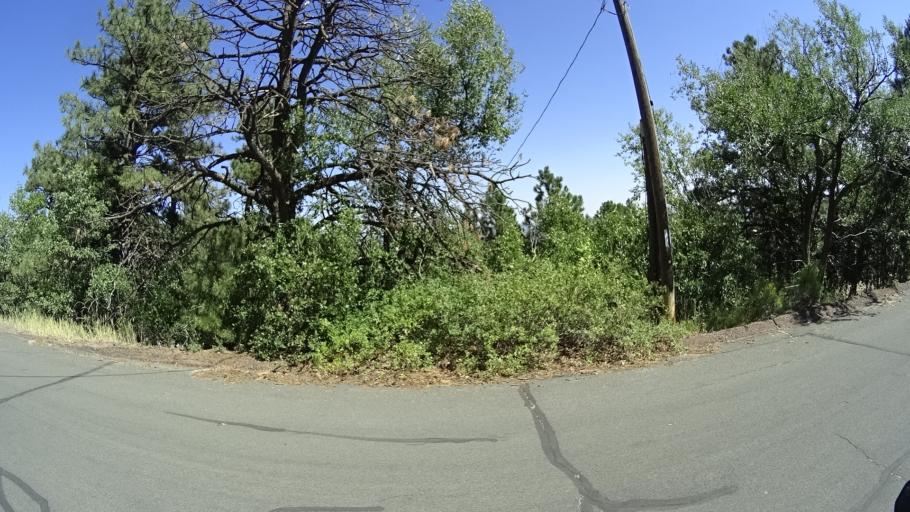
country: US
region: Colorado
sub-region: El Paso County
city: Colorado Springs
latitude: 38.7753
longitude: -104.8506
